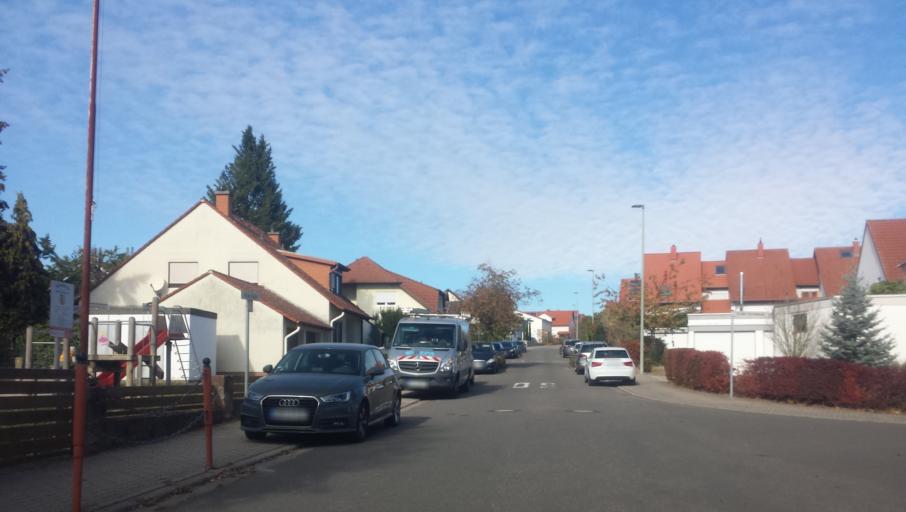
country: DE
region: Rheinland-Pfalz
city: Edenkoben
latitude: 49.2854
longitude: 8.1218
